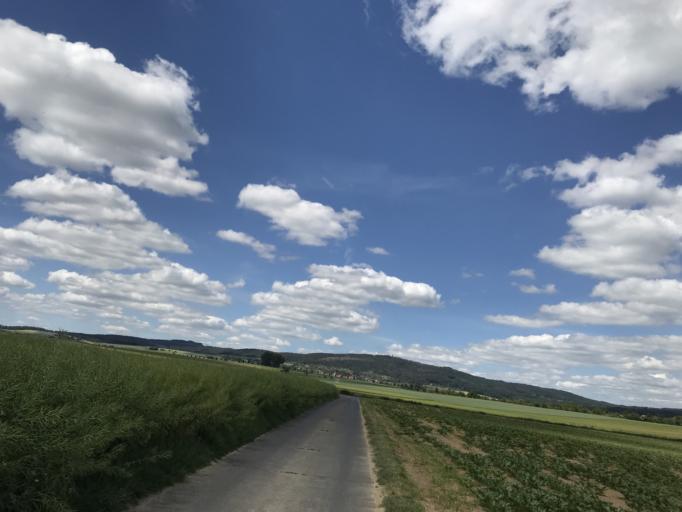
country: DE
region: Hesse
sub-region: Regierungsbezirk Darmstadt
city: Ober-Morlen
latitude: 50.3946
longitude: 8.6742
